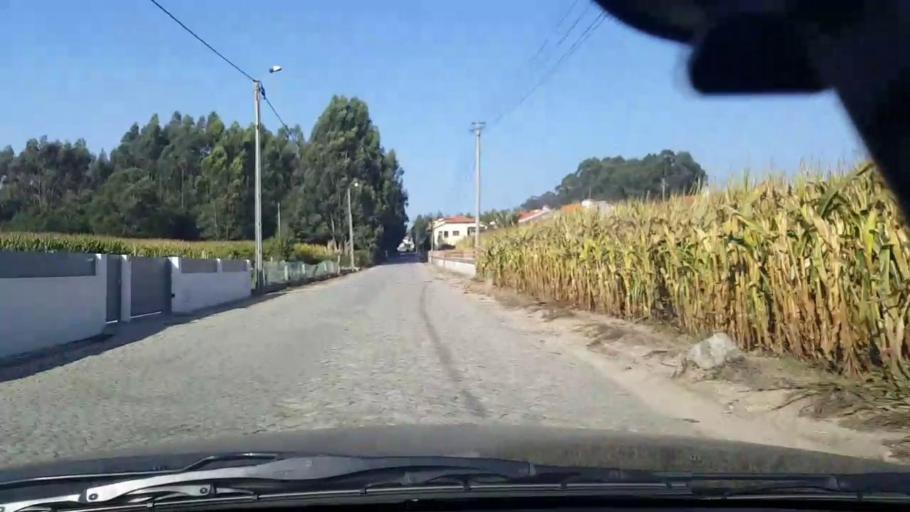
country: PT
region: Porto
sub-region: Matosinhos
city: Lavra
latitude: 41.2665
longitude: -8.6825
